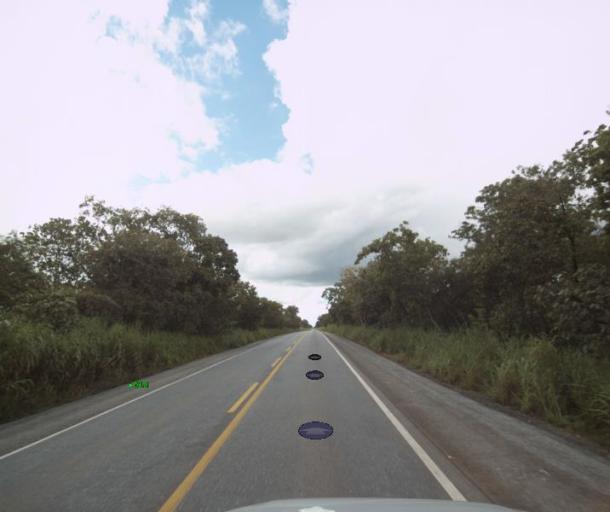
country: BR
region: Goias
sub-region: Porangatu
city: Porangatu
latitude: -13.2780
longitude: -49.1291
